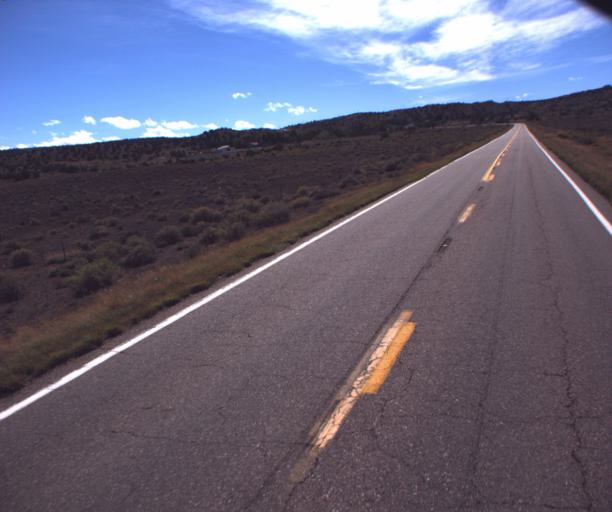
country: US
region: Arizona
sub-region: Apache County
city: Saint Johns
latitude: 34.4707
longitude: -109.6115
